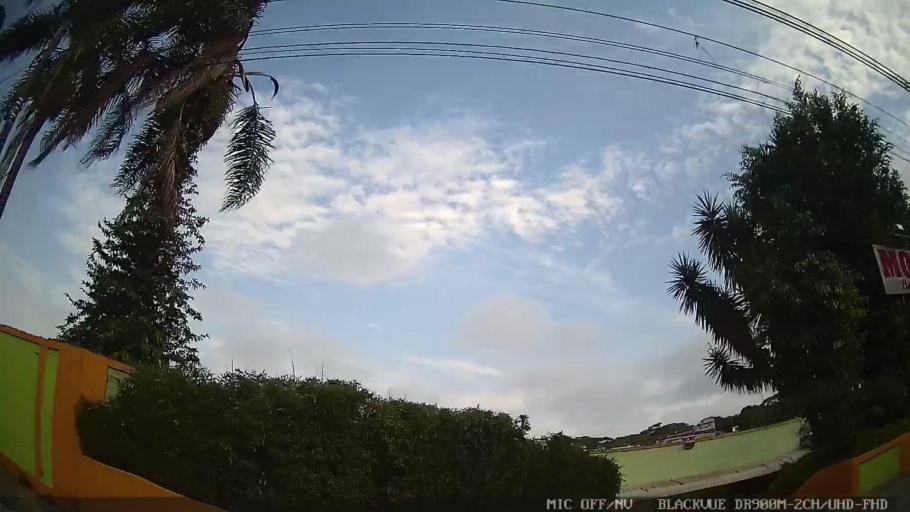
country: BR
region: Sao Paulo
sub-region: Ferraz De Vasconcelos
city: Ferraz de Vasconcelos
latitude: -23.5322
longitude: -46.3978
